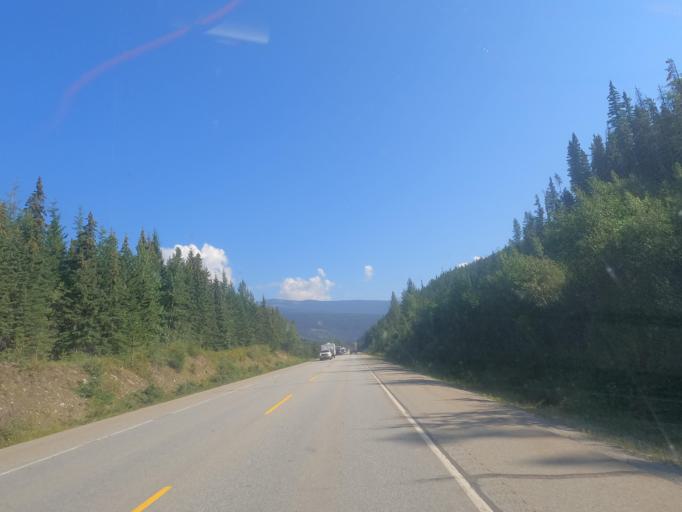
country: CA
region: Alberta
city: Jasper Park Lodge
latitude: 52.8732
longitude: -118.5003
